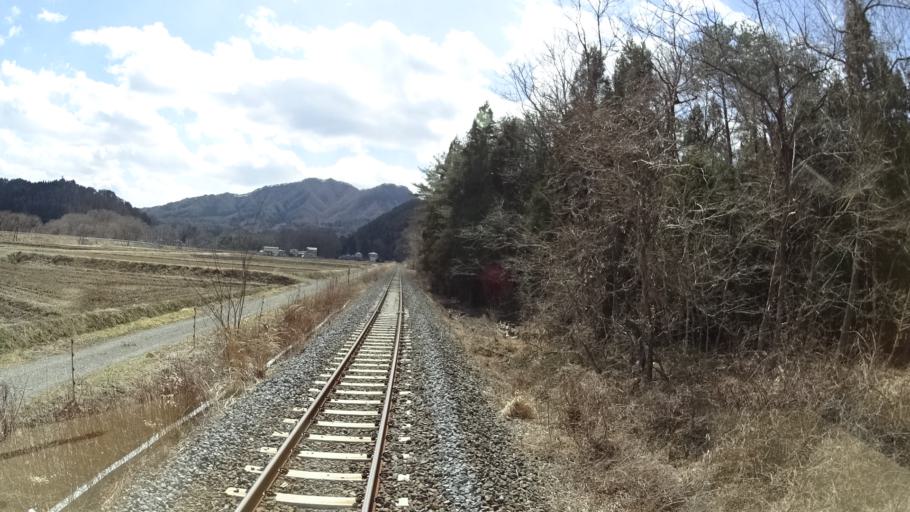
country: JP
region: Iwate
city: Yamada
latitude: 39.5219
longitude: 141.9174
